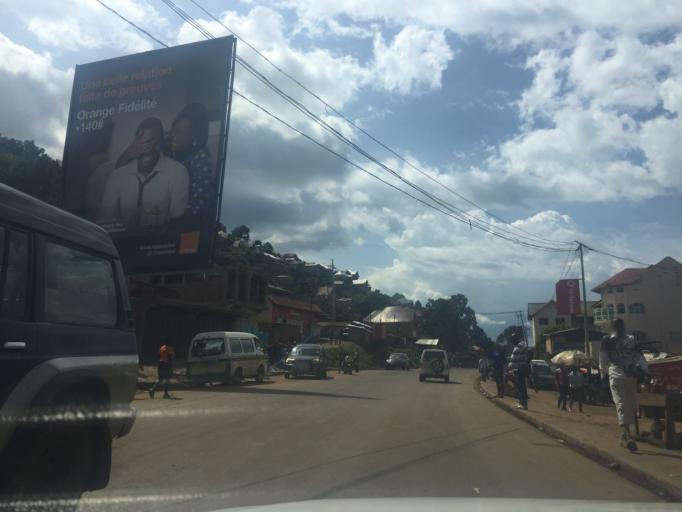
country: CD
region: South Kivu
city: Bukavu
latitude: -2.4885
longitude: 28.8475
